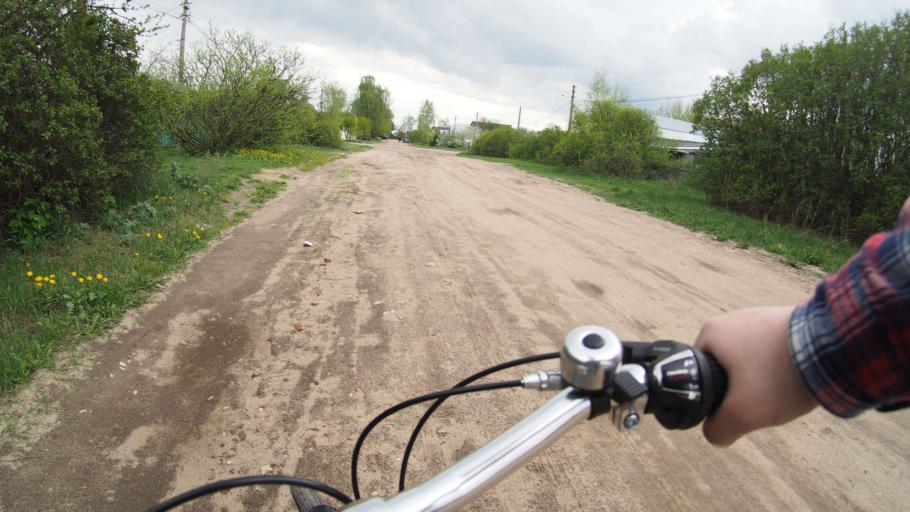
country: RU
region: Moskovskaya
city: Ramenskoye
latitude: 55.5555
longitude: 38.2344
